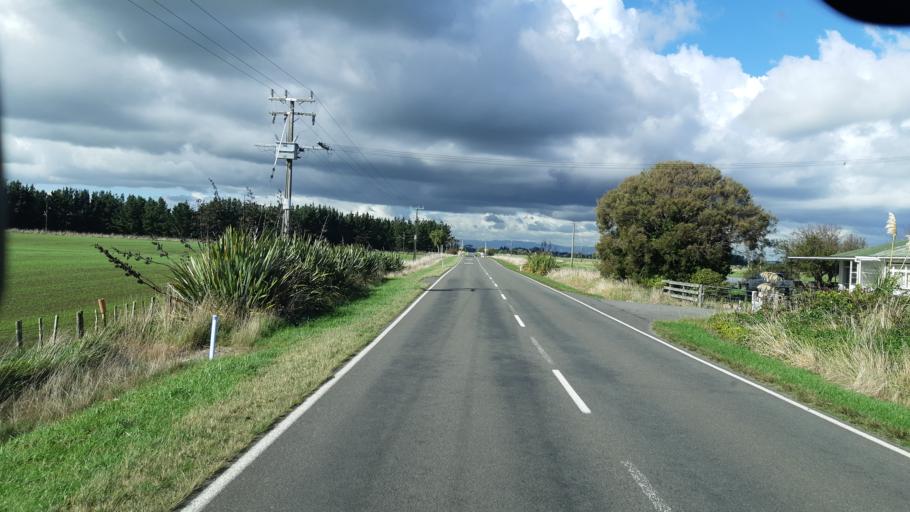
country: NZ
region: Manawatu-Wanganui
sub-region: Rangitikei District
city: Bulls
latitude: -40.1028
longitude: 175.3977
